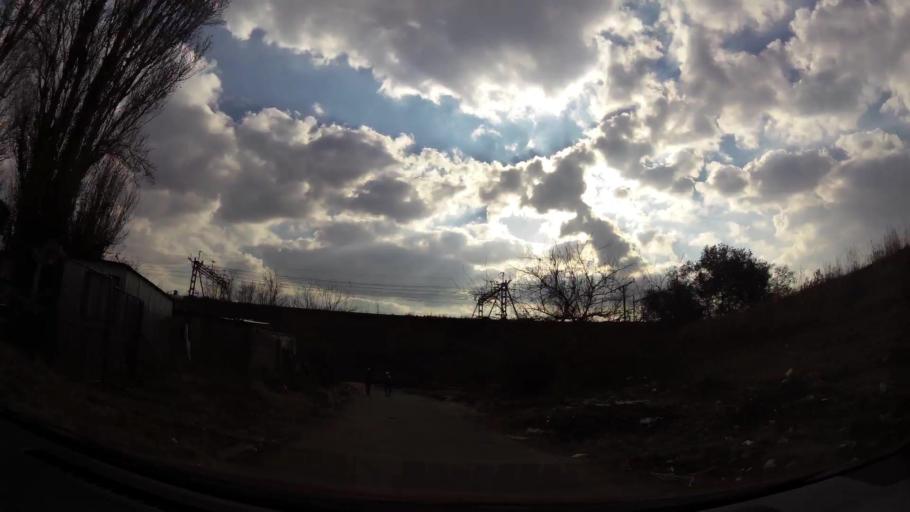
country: ZA
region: Gauteng
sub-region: City of Johannesburg Metropolitan Municipality
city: Roodepoort
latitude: -26.2220
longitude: 27.9333
